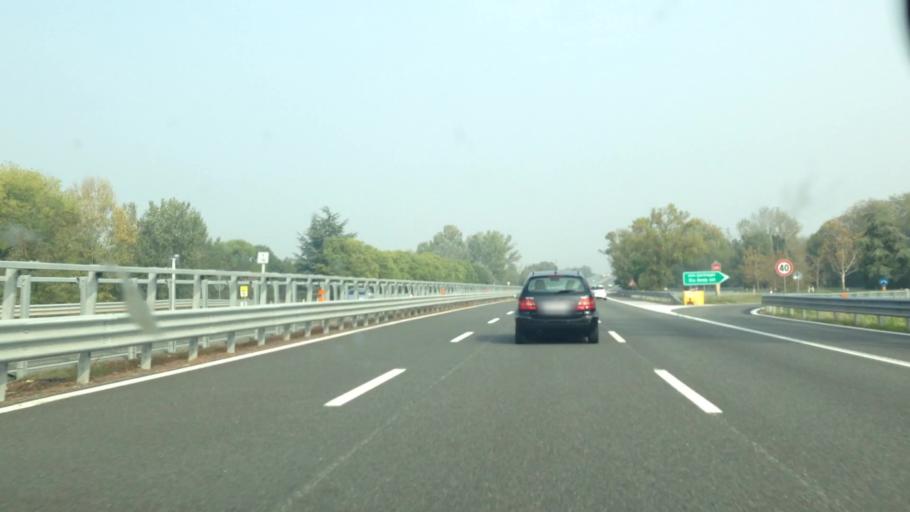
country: IT
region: Piedmont
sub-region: Provincia di Alessandria
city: Mirabello Monferrato
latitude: 45.0162
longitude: 8.5354
